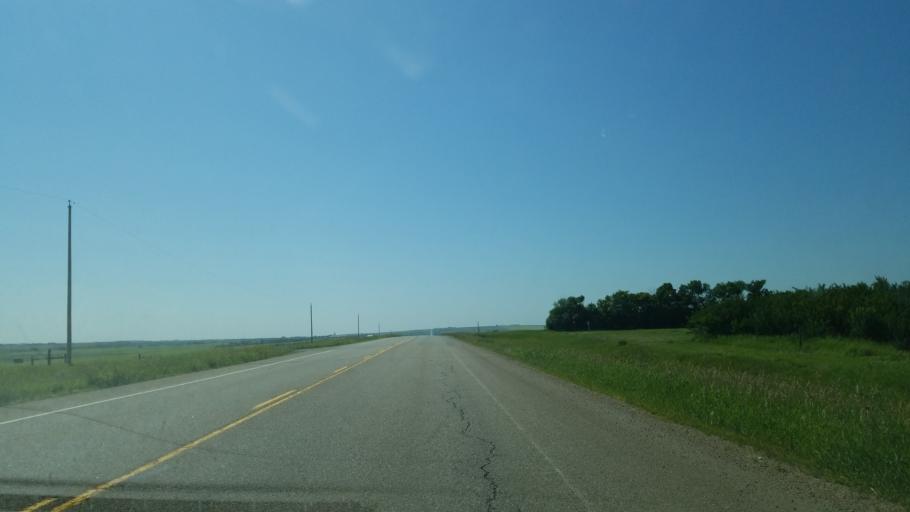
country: CA
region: Saskatchewan
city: Macklin
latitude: 52.3613
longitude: -110.0402
